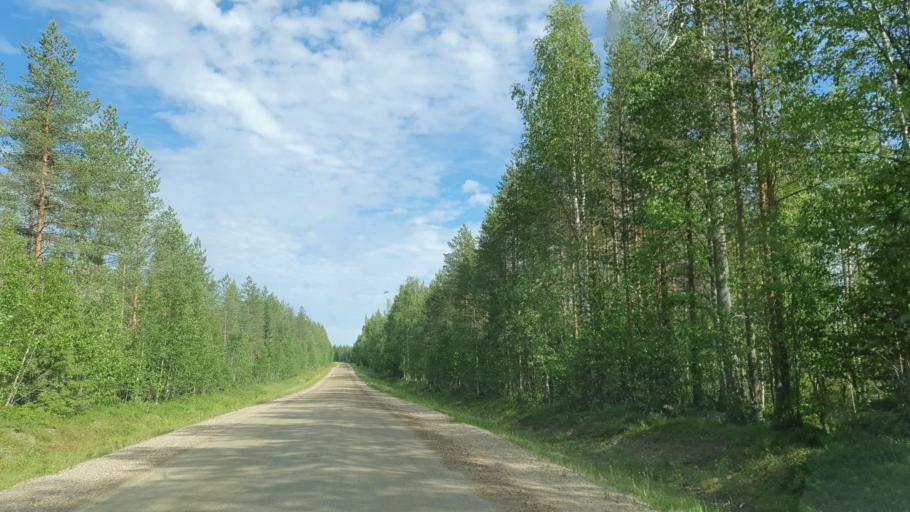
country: FI
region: Kainuu
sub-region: Kehys-Kainuu
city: Kuhmo
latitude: 64.5141
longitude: 29.4194
